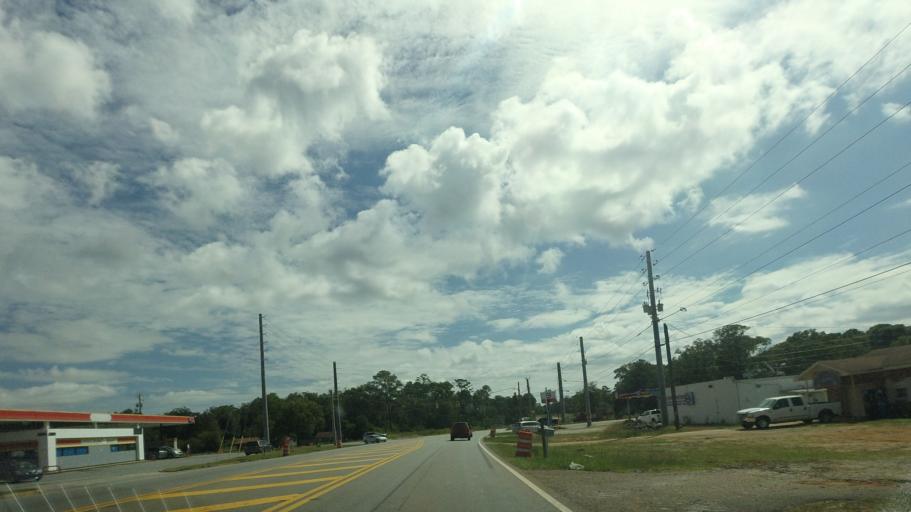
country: US
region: Georgia
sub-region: Houston County
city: Robins Air Force Base
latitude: 32.5544
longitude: -83.6255
